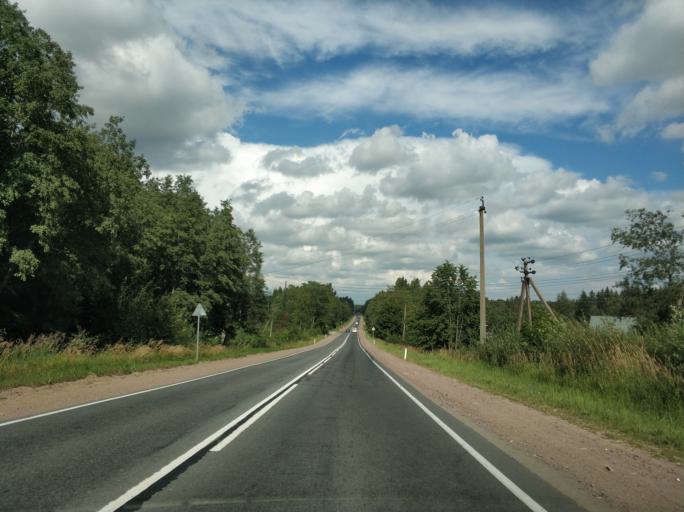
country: RU
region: Leningrad
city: Romanovka
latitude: 60.0706
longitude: 30.7437
